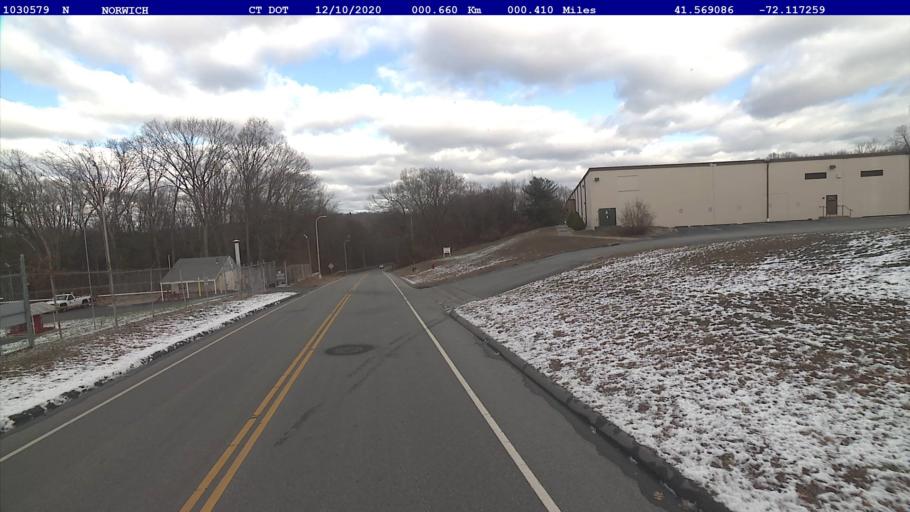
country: US
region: Connecticut
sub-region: New London County
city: Baltic
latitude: 41.5691
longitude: -72.1171
